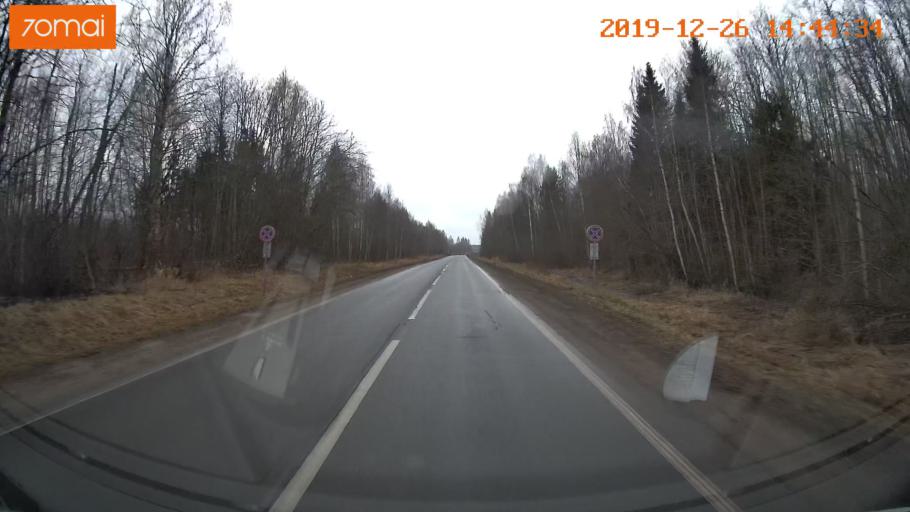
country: RU
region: Jaroslavl
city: Poshekhon'ye
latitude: 58.3464
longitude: 39.0510
